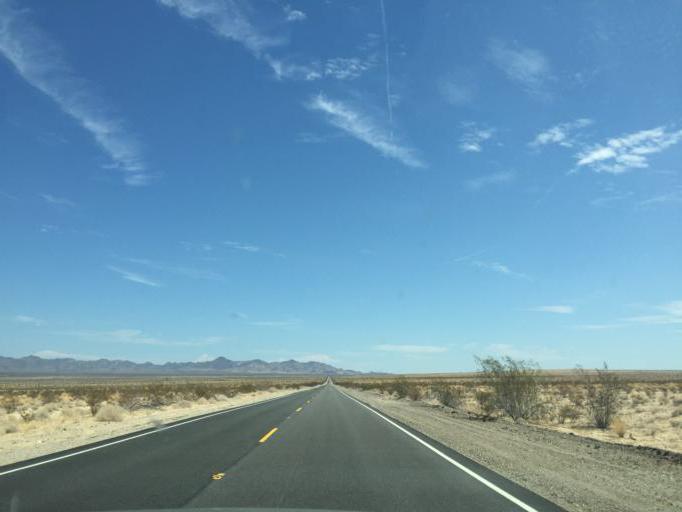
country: US
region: California
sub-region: Riverside County
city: Mesa Verde
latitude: 34.1002
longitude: -115.0002
